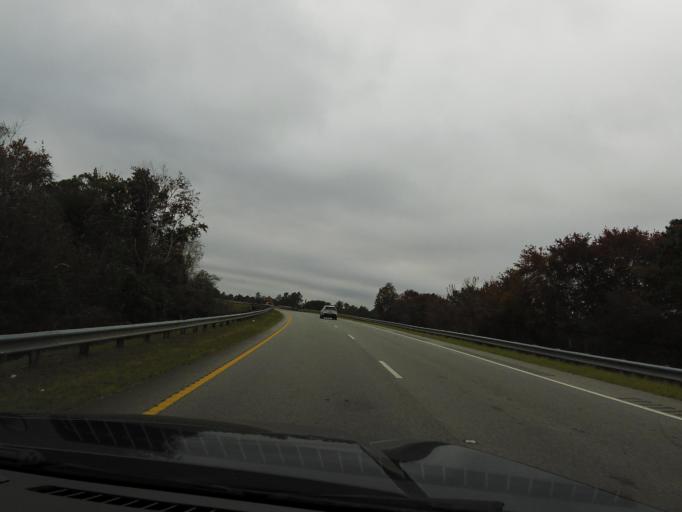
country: US
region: Georgia
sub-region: Charlton County
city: Folkston
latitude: 30.8710
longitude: -82.0138
